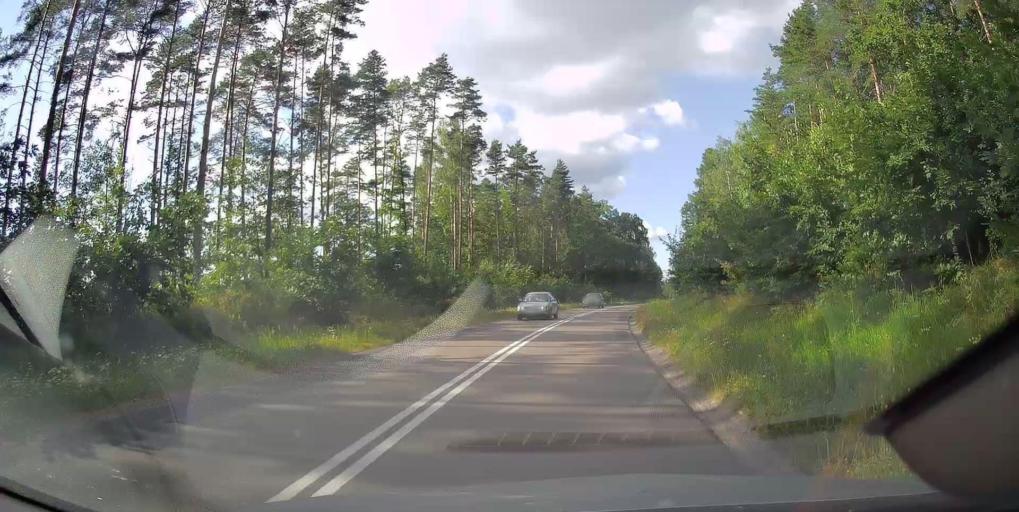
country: PL
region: Swietokrzyskie
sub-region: Powiat skarzyski
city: Suchedniow
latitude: 51.0125
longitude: 20.8403
